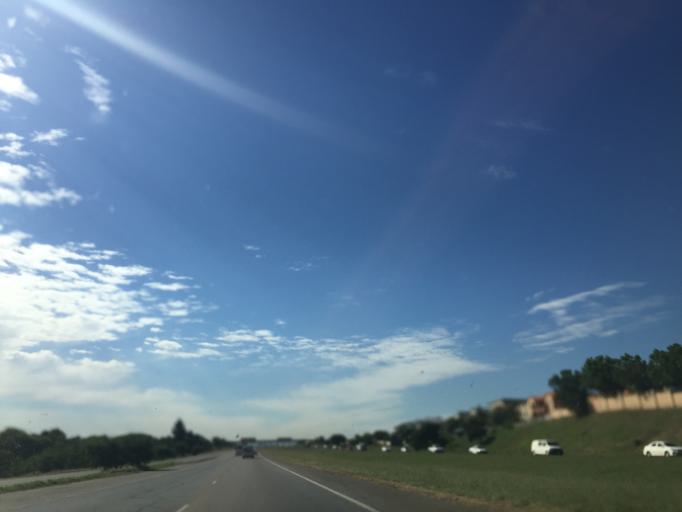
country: ZA
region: Gauteng
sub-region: Ekurhuleni Metropolitan Municipality
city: Germiston
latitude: -26.2892
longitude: 28.1031
